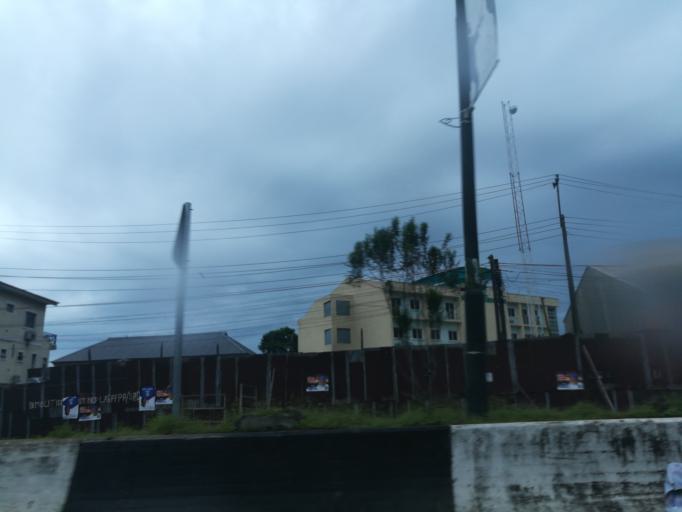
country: NG
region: Lagos
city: Makoko
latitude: 6.5029
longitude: 3.3773
